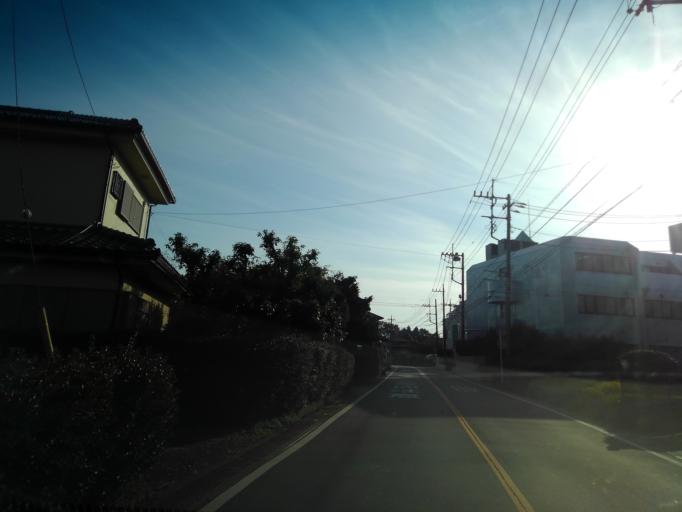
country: JP
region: Saitama
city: Tokorozawa
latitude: 35.7942
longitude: 139.4189
